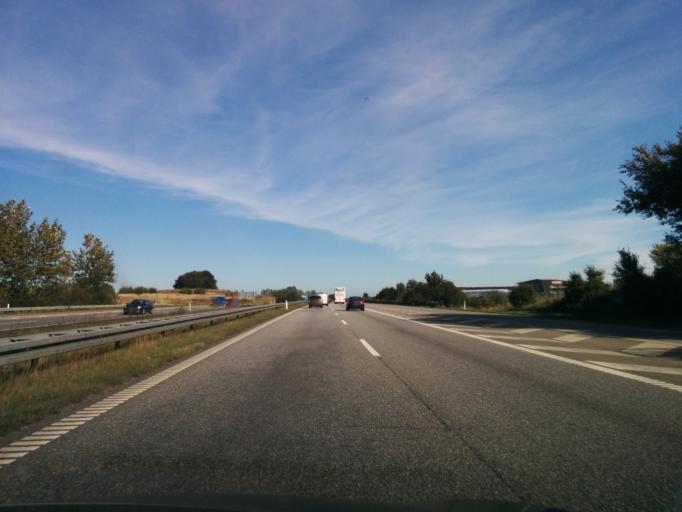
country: DK
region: Central Jutland
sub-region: Skanderborg Kommune
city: Stilling
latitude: 56.0685
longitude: 9.9817
